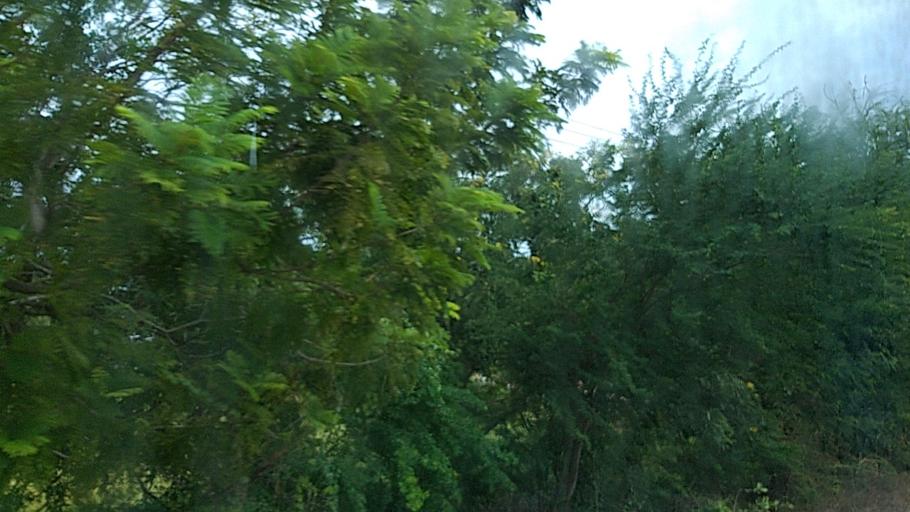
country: TH
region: Maha Sarakham
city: Maha Sarakham
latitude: 16.1586
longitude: 103.3625
